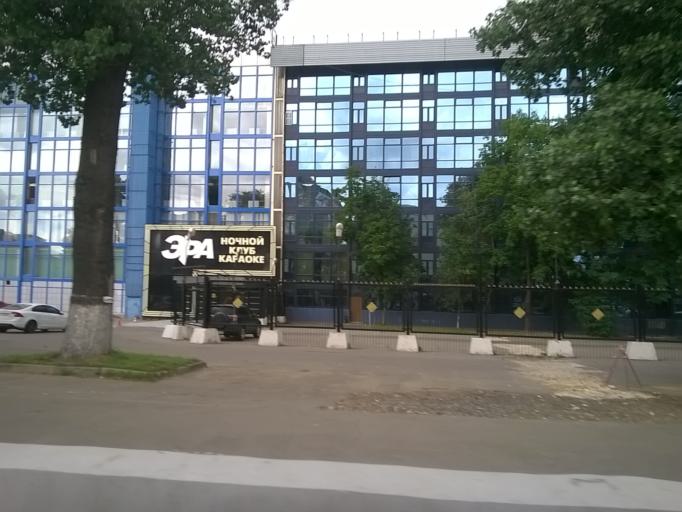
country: RU
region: Moscow
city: Lefortovo
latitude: 55.7492
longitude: 37.7031
